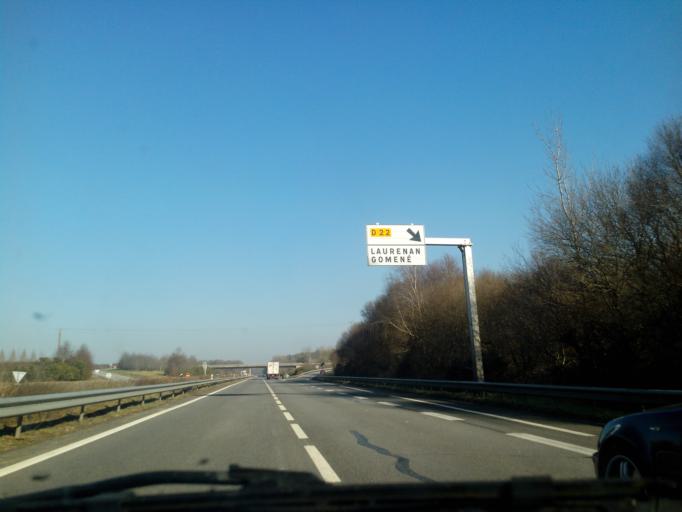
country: FR
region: Brittany
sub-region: Departement des Cotes-d'Armor
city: Plemet
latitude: 48.1898
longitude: -2.5191
